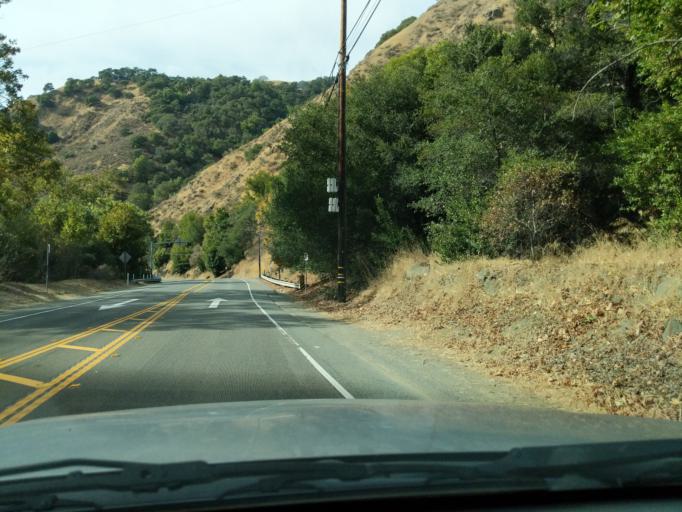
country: US
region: California
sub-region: Alameda County
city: Fremont
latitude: 37.5980
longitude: -121.9473
